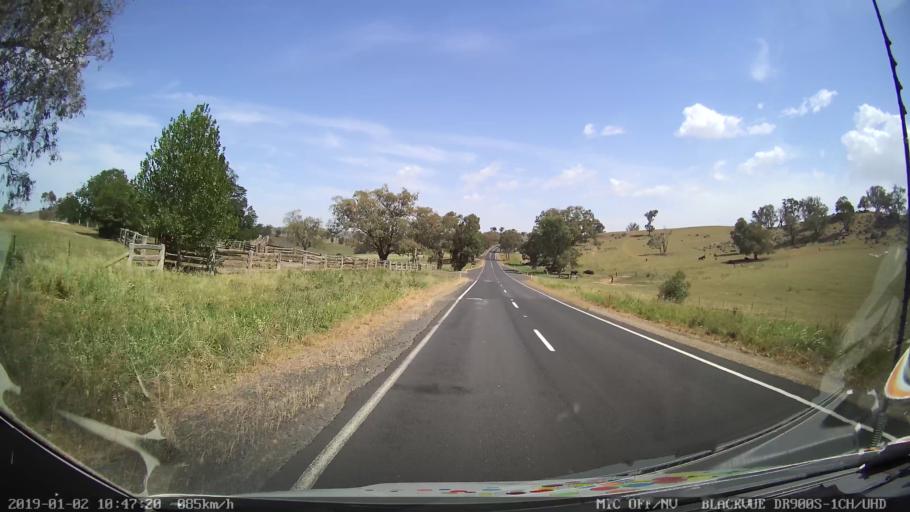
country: AU
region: New South Wales
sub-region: Cootamundra
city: Cootamundra
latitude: -34.7461
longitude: 148.2744
